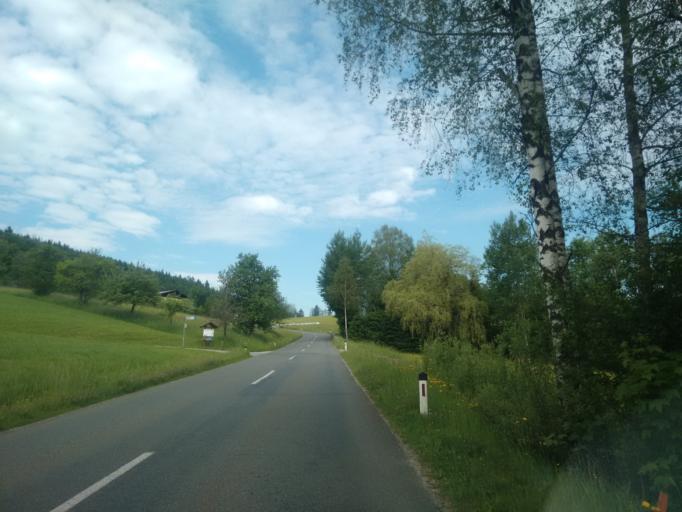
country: AT
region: Upper Austria
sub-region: Politischer Bezirk Kirchdorf an der Krems
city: Rossleithen
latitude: 47.6970
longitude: 14.3023
